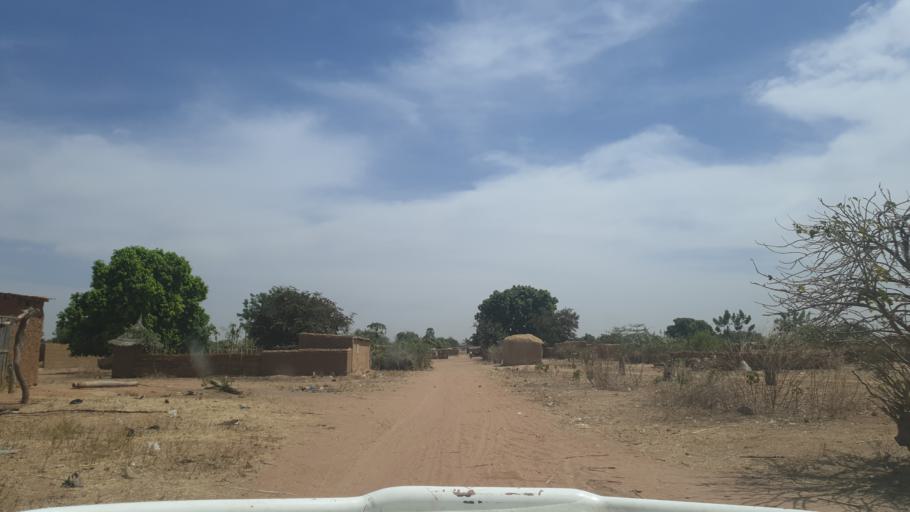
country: ML
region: Sikasso
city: Yorosso
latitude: 12.2913
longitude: -4.6534
